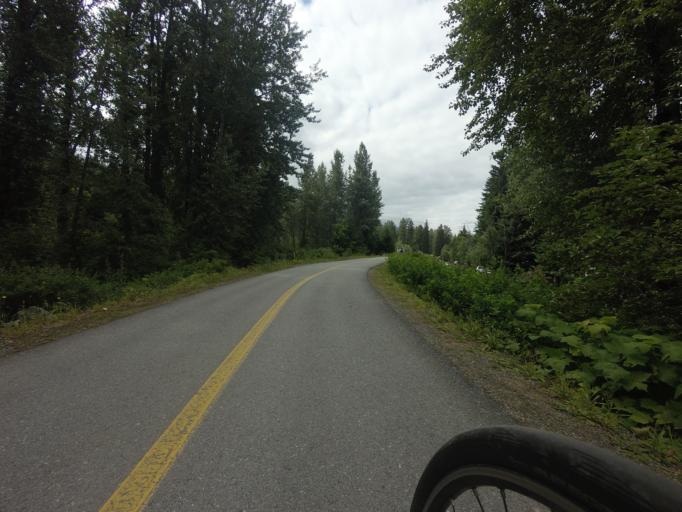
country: CA
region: British Columbia
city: Whistler
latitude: 50.1382
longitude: -122.9499
